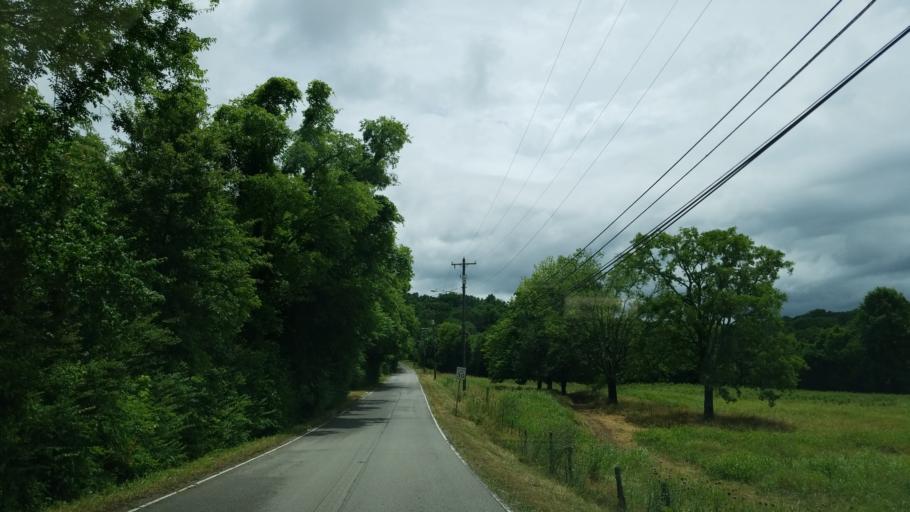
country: US
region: Tennessee
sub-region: Rutherford County
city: La Vergne
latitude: 36.1131
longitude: -86.6475
